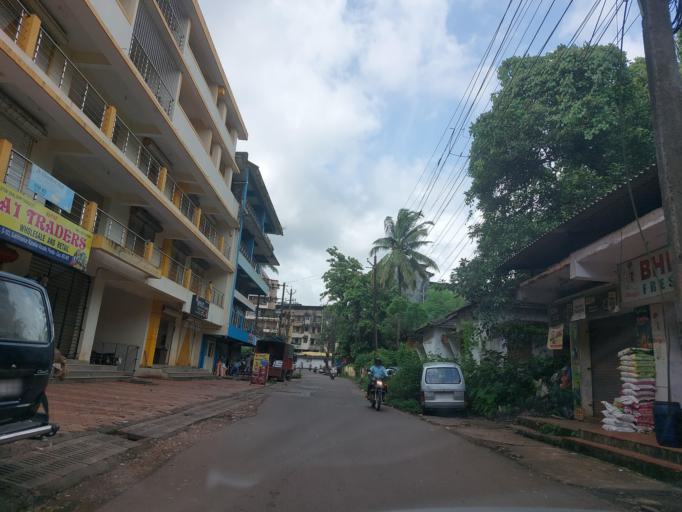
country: IN
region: Goa
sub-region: North Goa
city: Ponda
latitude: 15.4014
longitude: 74.0099
